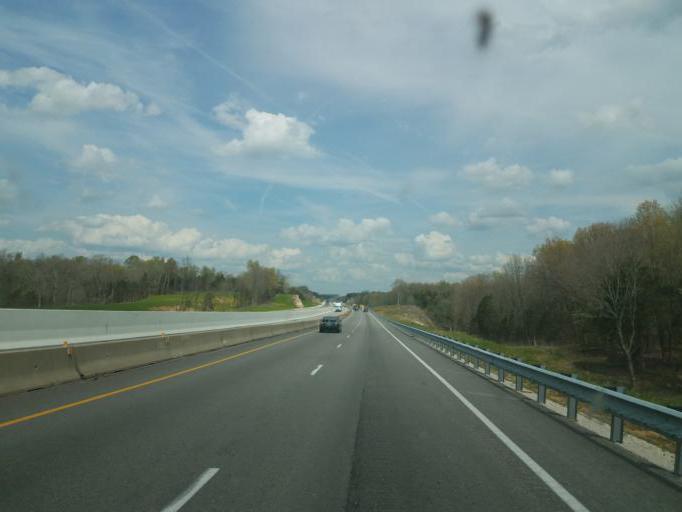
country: US
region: Kentucky
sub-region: Hart County
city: Munfordville
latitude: 37.4074
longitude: -85.8812
